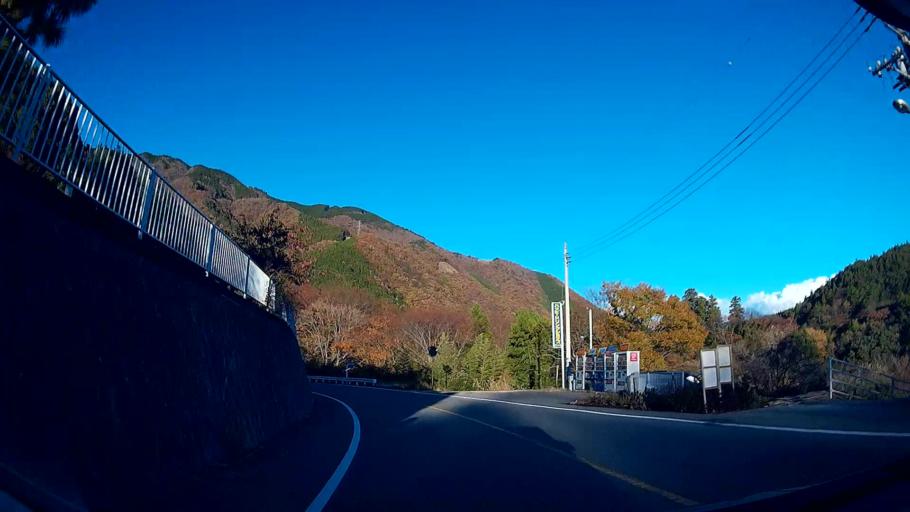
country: JP
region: Yamanashi
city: Uenohara
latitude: 35.5331
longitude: 139.0530
